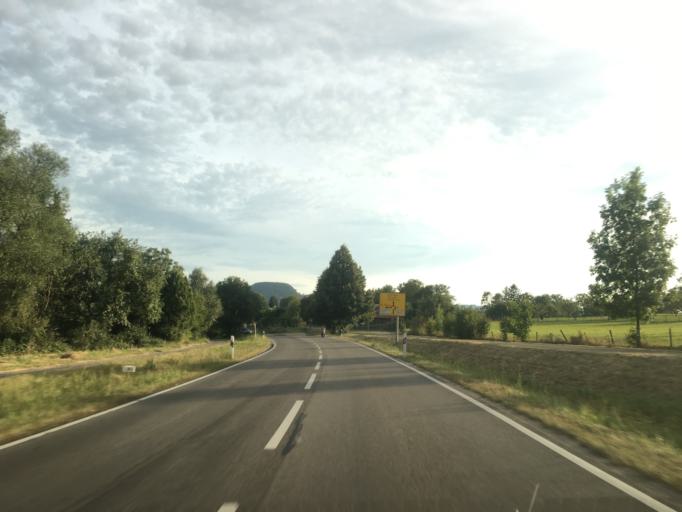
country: DE
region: Baden-Wuerttemberg
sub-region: Tuebingen Region
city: Eningen unter Achalm
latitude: 48.4969
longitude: 9.2654
